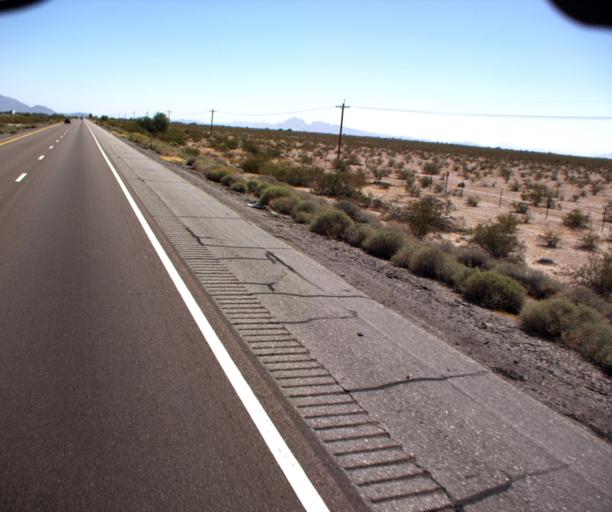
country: US
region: Arizona
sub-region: La Paz County
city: Salome
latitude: 33.5597
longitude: -113.2934
